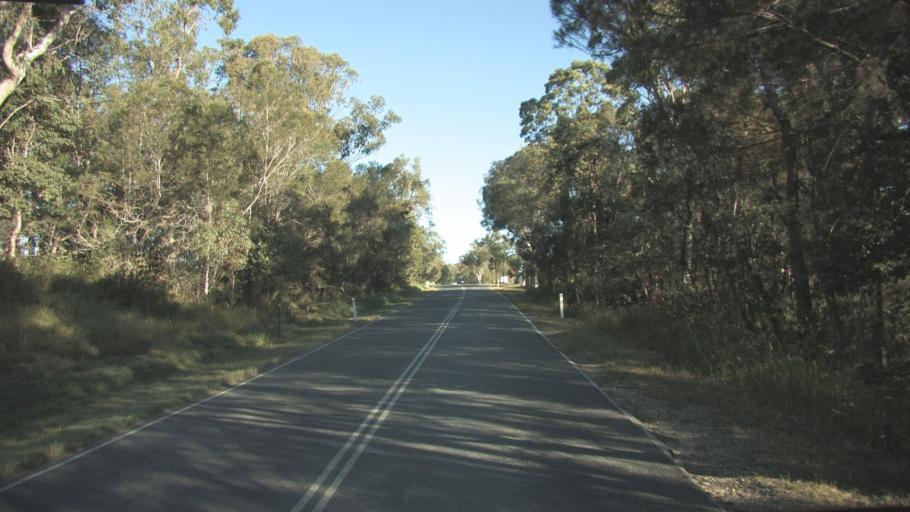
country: AU
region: Queensland
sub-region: Logan
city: Logan Reserve
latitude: -27.7240
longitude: 153.0901
